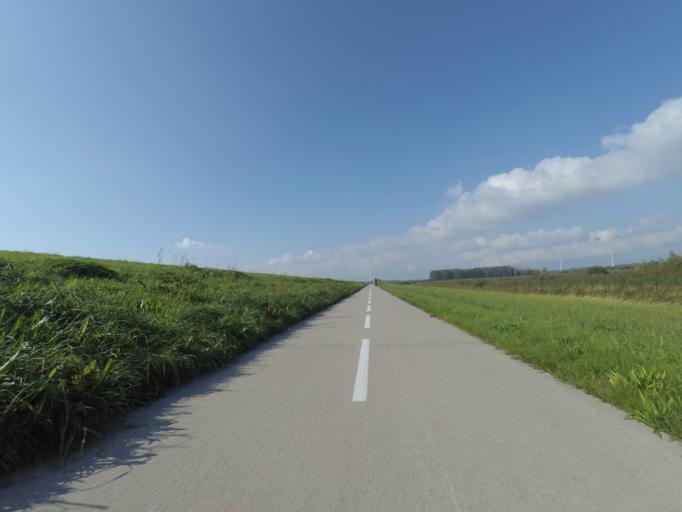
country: NL
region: Flevoland
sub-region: Gemeente Zeewolde
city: Zeewolde
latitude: 52.3656
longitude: 5.5720
